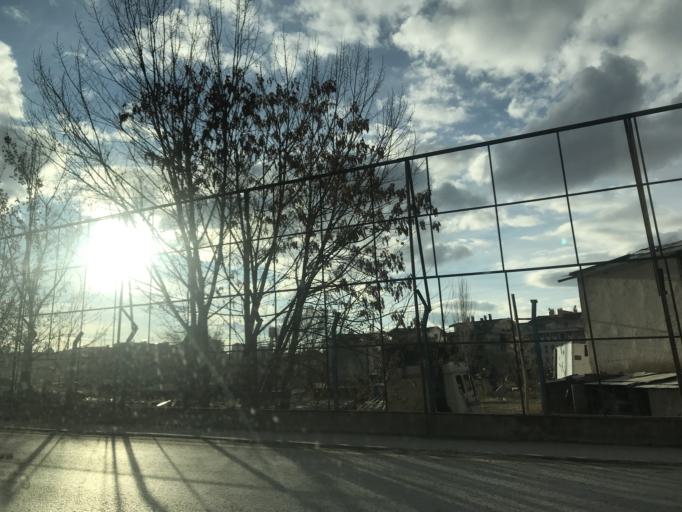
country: TR
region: Ankara
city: Mamak
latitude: 39.9781
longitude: 32.8856
